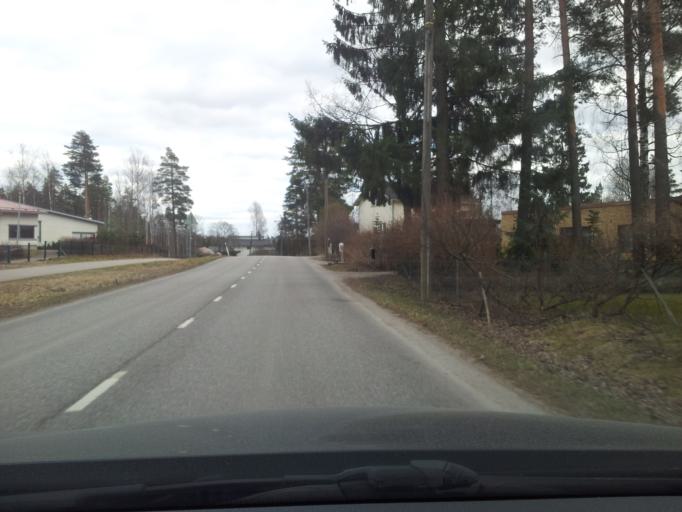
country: FI
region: Uusimaa
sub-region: Helsinki
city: Kilo
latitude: 60.2097
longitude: 24.8055
